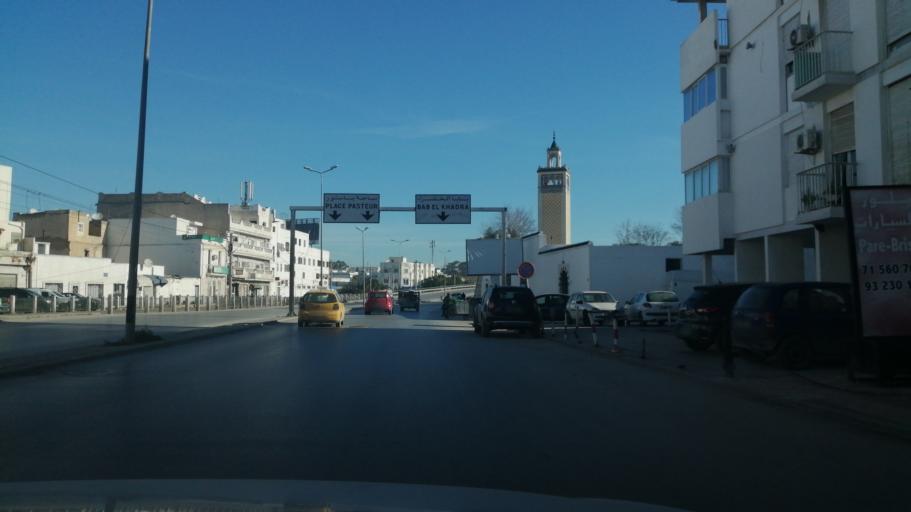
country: TN
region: Tunis
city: Tunis
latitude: 36.8119
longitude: 10.1665
